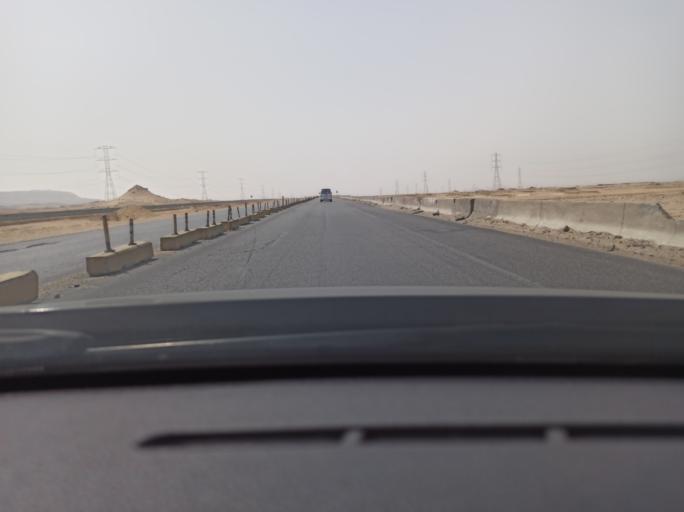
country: EG
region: Muhafazat Bani Suwayf
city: Bush
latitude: 29.1164
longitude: 31.2200
